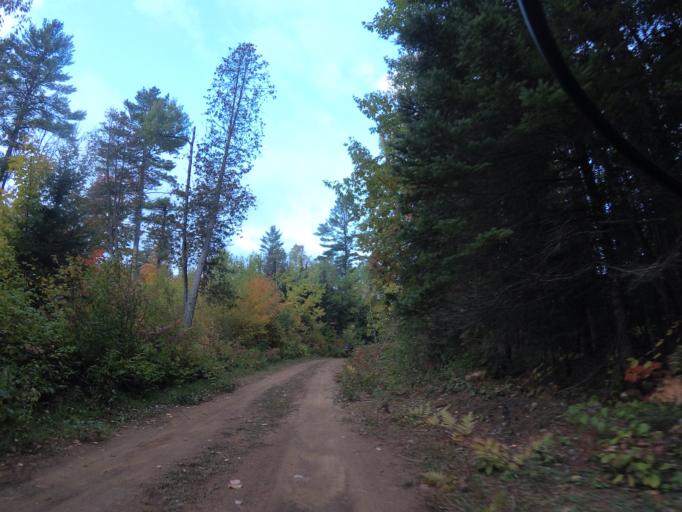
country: CA
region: Ontario
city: Pembroke
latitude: 45.3013
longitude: -77.2544
